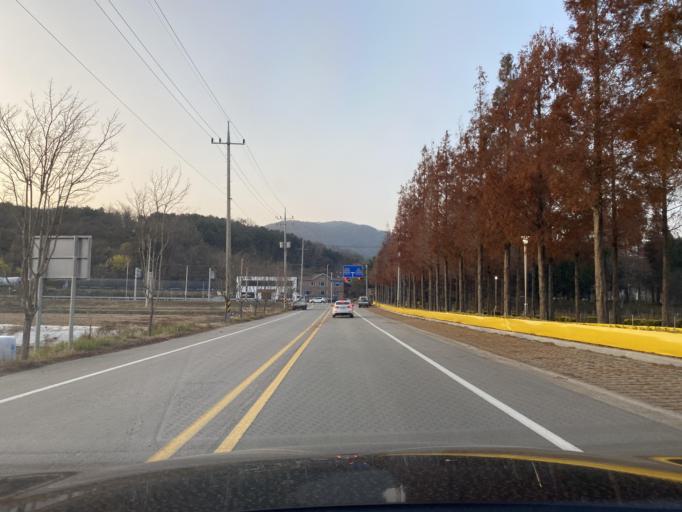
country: KR
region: Chungcheongnam-do
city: Hongsung
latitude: 36.6887
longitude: 126.6574
